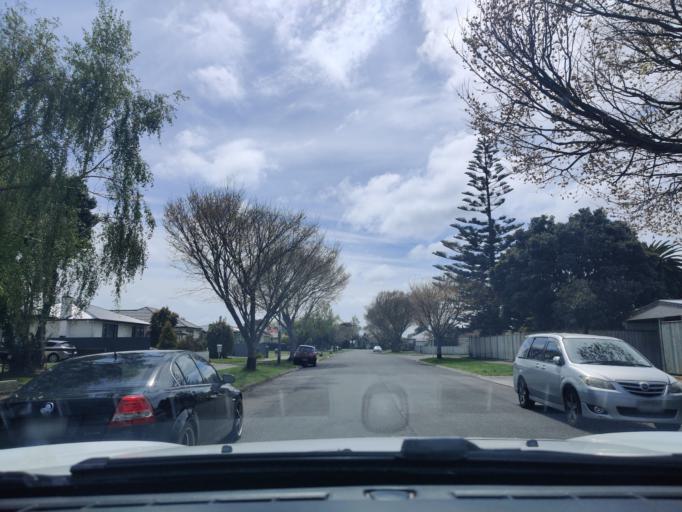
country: NZ
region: Manawatu-Wanganui
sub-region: Palmerston North City
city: Palmerston North
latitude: -40.3512
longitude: 175.5895
